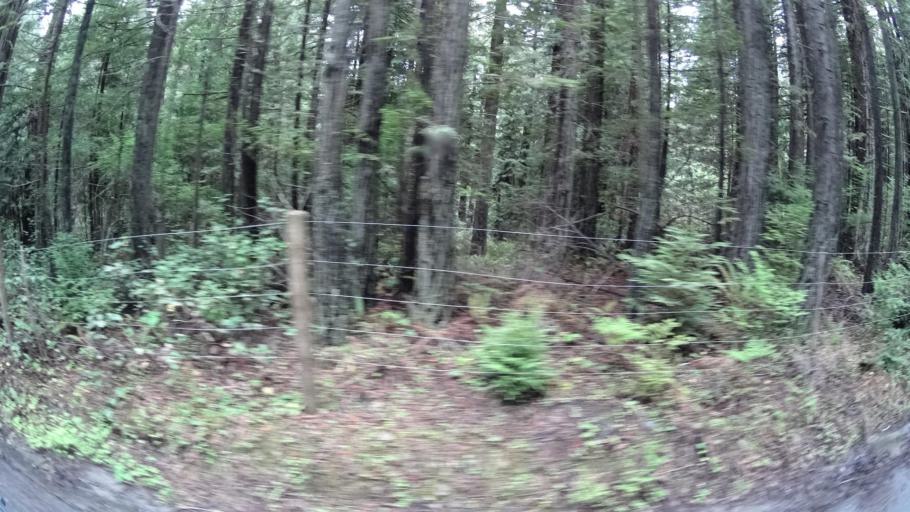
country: US
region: California
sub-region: Humboldt County
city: Blue Lake
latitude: 40.9046
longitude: -123.9762
